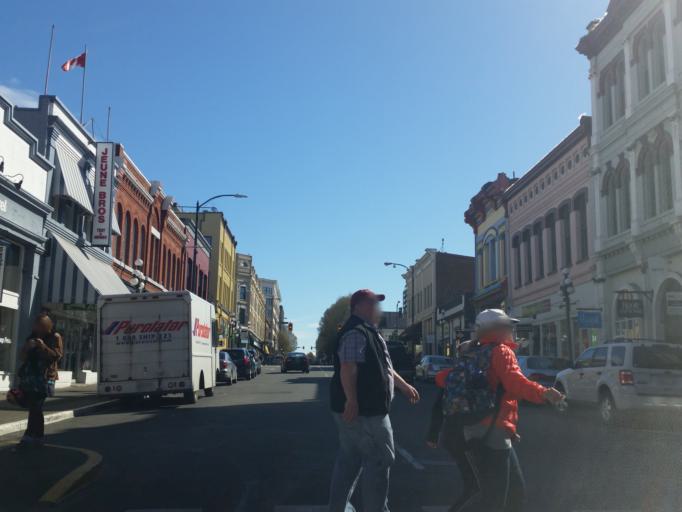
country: CA
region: British Columbia
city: Victoria
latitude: 48.4277
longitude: -123.3685
